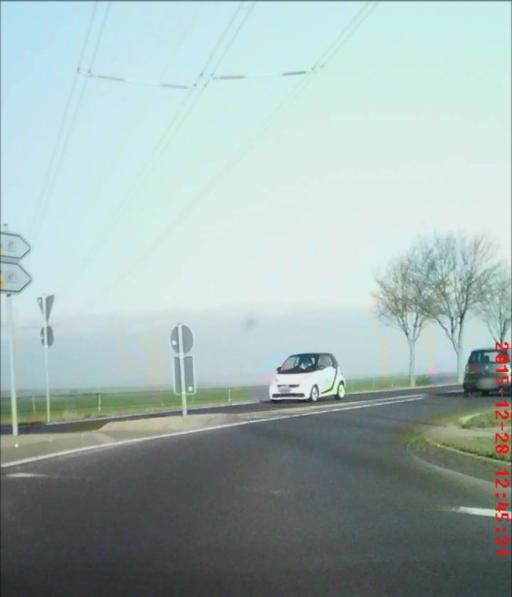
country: DE
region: Thuringia
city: Niederrossla
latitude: 51.0141
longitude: 11.4704
